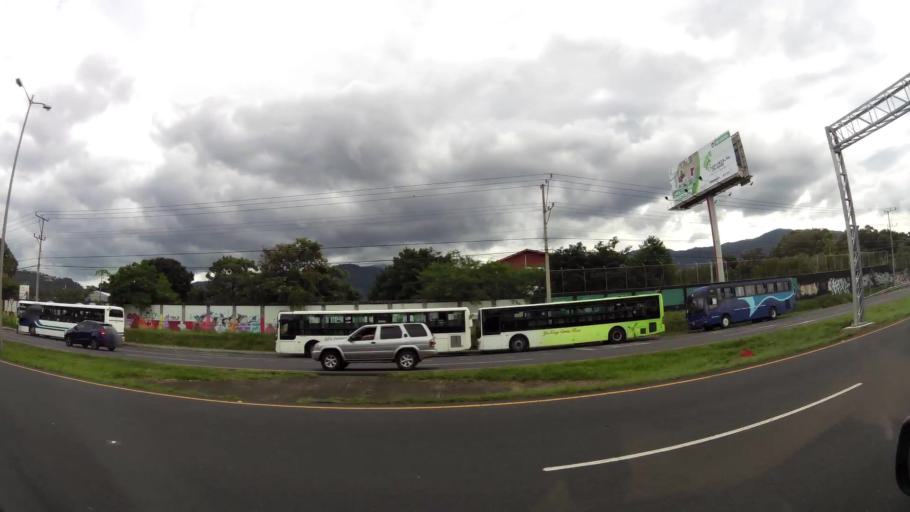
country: CR
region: San Jose
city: Santa Ana
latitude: 9.9456
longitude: -84.1888
